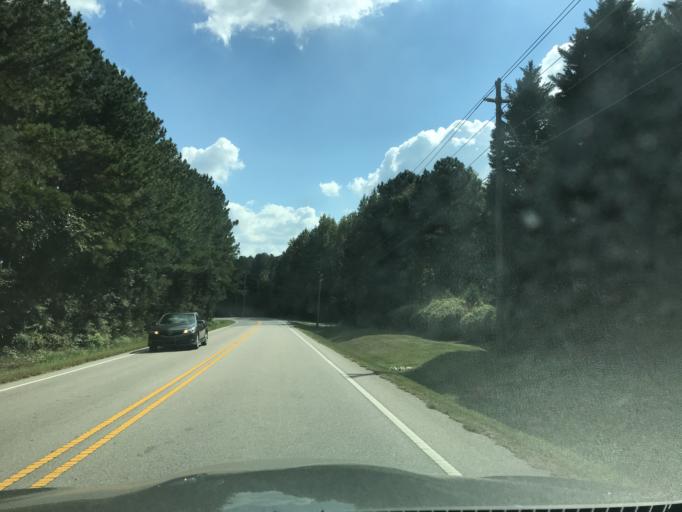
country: US
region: North Carolina
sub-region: Wake County
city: Wake Forest
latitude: 35.9128
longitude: -78.5294
